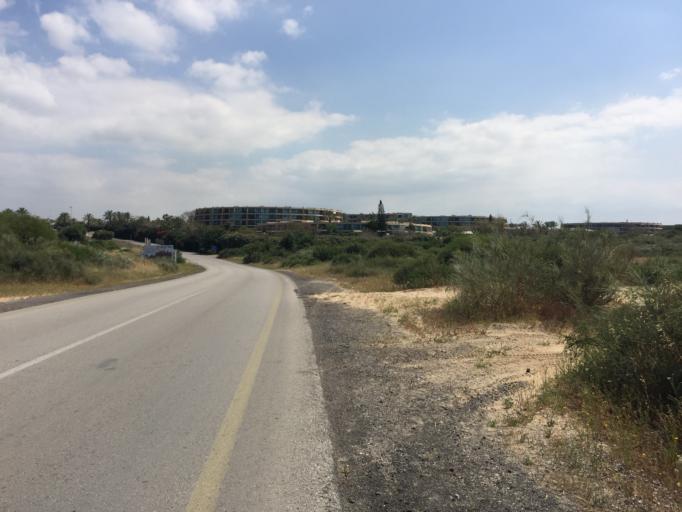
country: IL
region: Haifa
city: Qesarya
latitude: 32.4915
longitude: 34.8999
